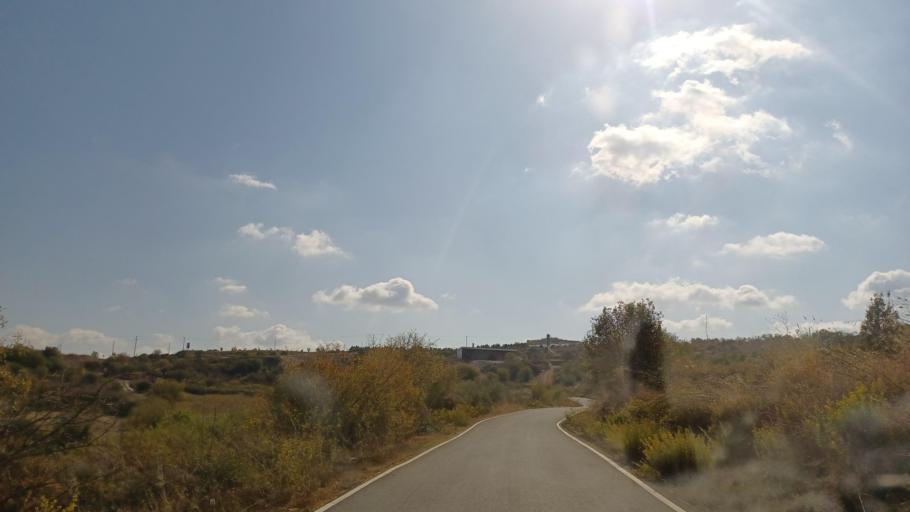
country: CY
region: Pafos
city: Tala
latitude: 34.9118
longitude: 32.4643
